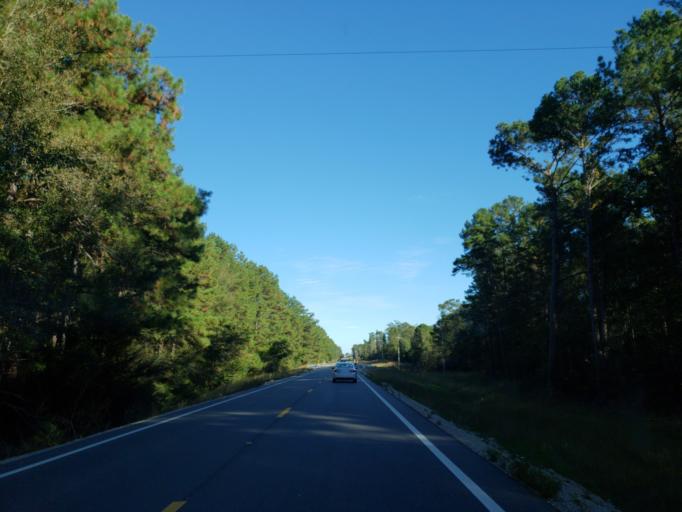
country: US
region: Mississippi
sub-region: Perry County
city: Richton
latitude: 31.3646
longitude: -89.0541
